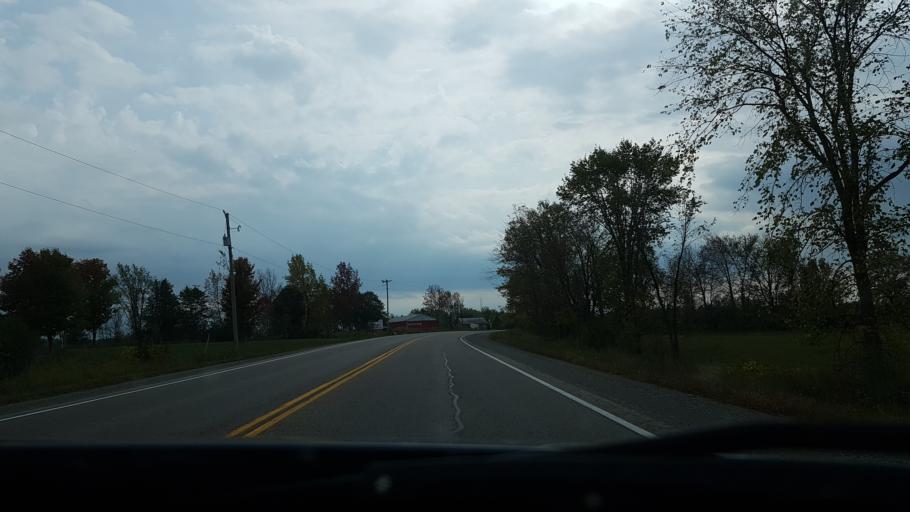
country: CA
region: Ontario
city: Omemee
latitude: 44.4651
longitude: -78.7622
